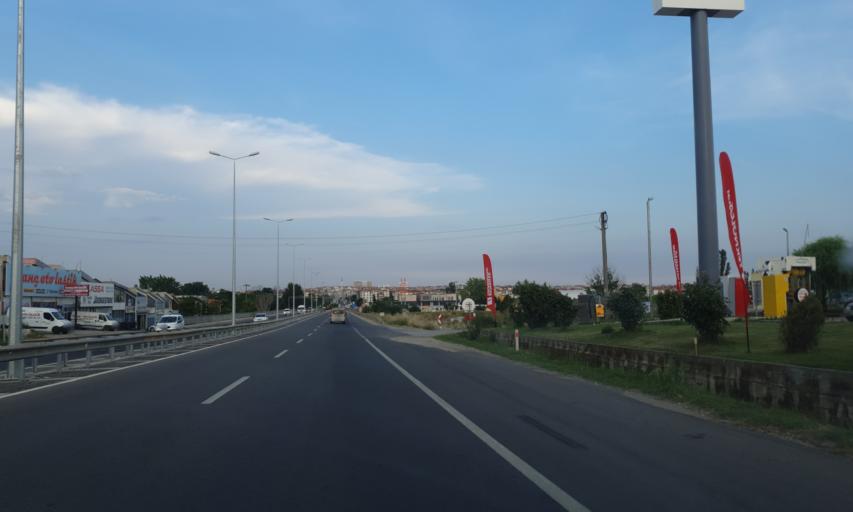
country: TR
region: Kirklareli
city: Luleburgaz
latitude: 41.4051
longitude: 27.3387
